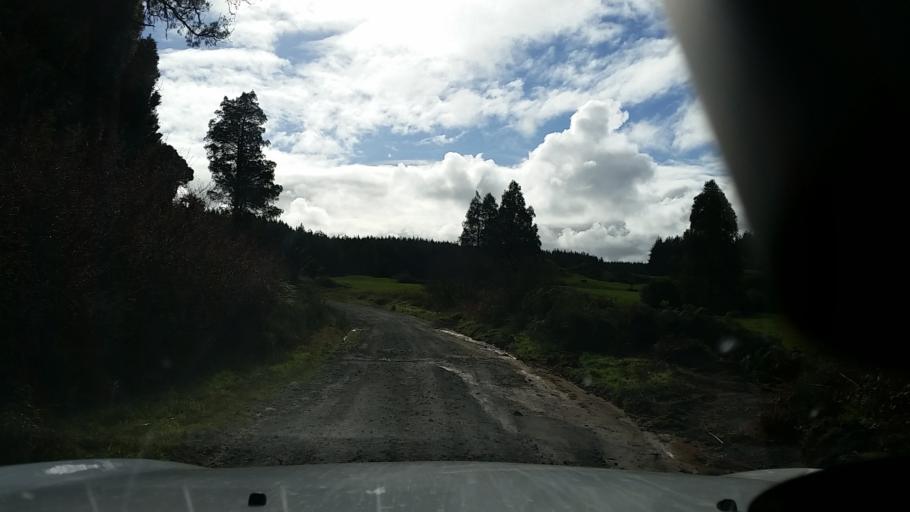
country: NZ
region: Bay of Plenty
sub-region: Rotorua District
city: Rotorua
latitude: -38.0760
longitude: 176.0363
